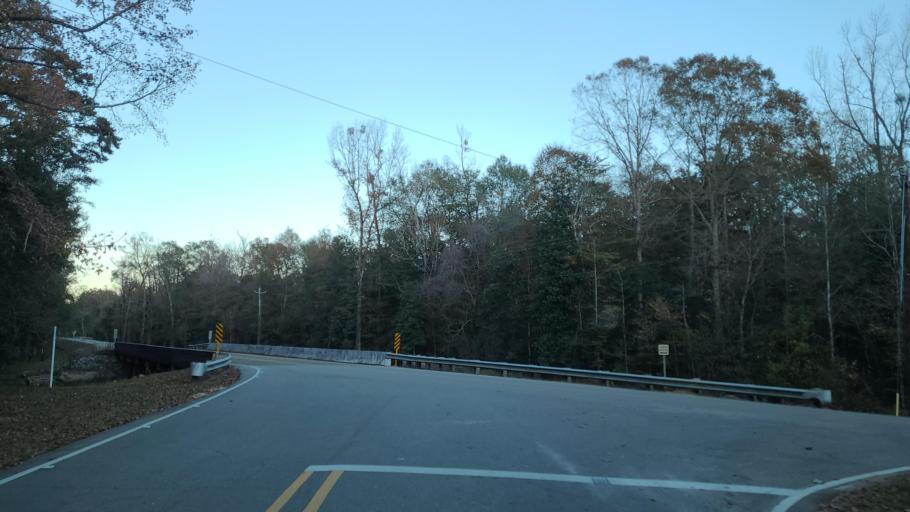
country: US
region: Mississippi
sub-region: Stone County
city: Wiggins
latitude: 31.0501
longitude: -89.1952
